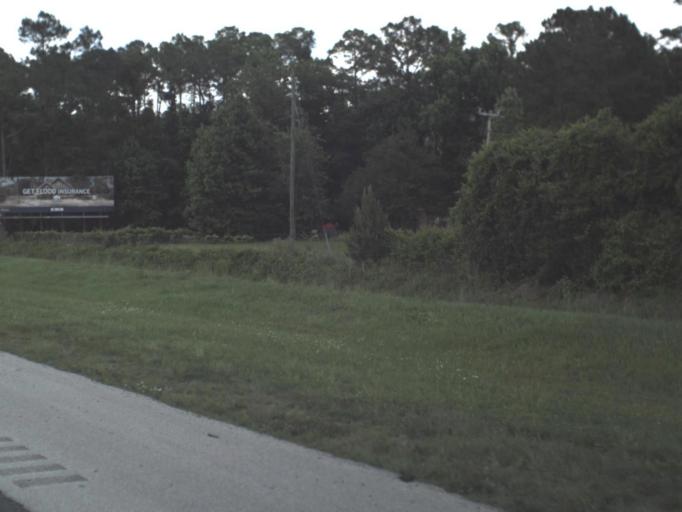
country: US
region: Florida
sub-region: Saint Johns County
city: Villano Beach
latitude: 29.9710
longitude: -81.4525
